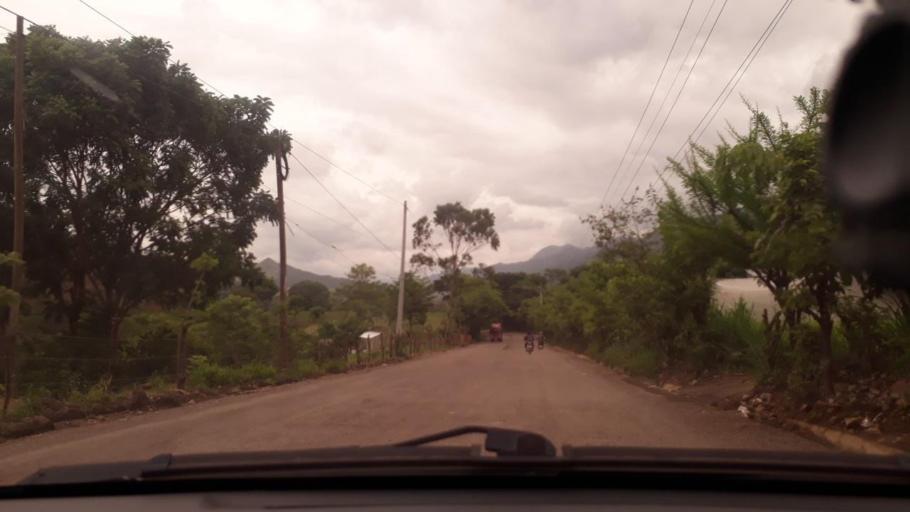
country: GT
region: Chiquimula
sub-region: Municipio de San Juan Ermita
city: San Juan Ermita
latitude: 14.7534
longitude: -89.4461
